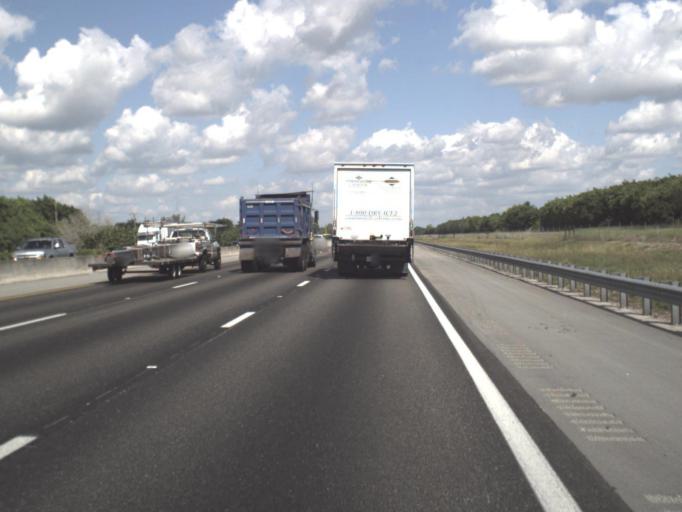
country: US
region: Florida
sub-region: Palm Beach County
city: Kings Point
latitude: 26.3989
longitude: -80.1711
